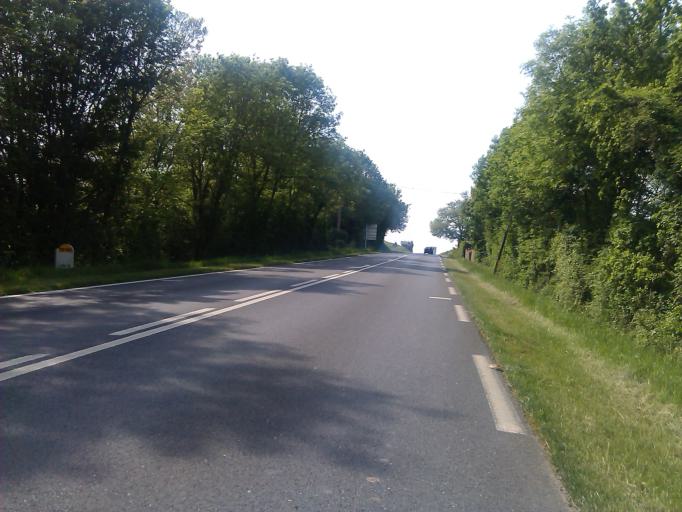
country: FR
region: Centre
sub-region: Departement de l'Indre
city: La Chatre
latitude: 46.5626
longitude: 2.0473
